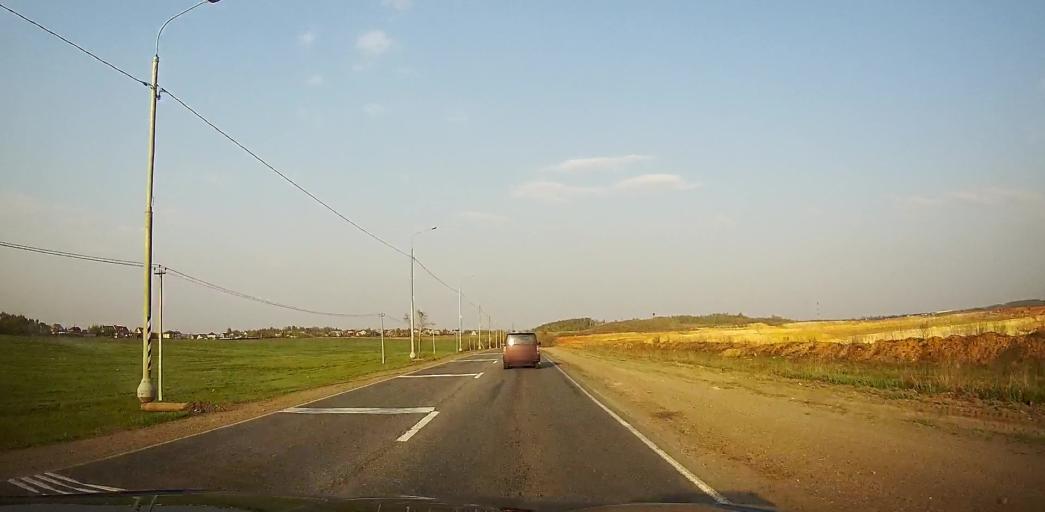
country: RU
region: Moskovskaya
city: Ostrovtsy
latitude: 55.5423
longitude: 38.0495
